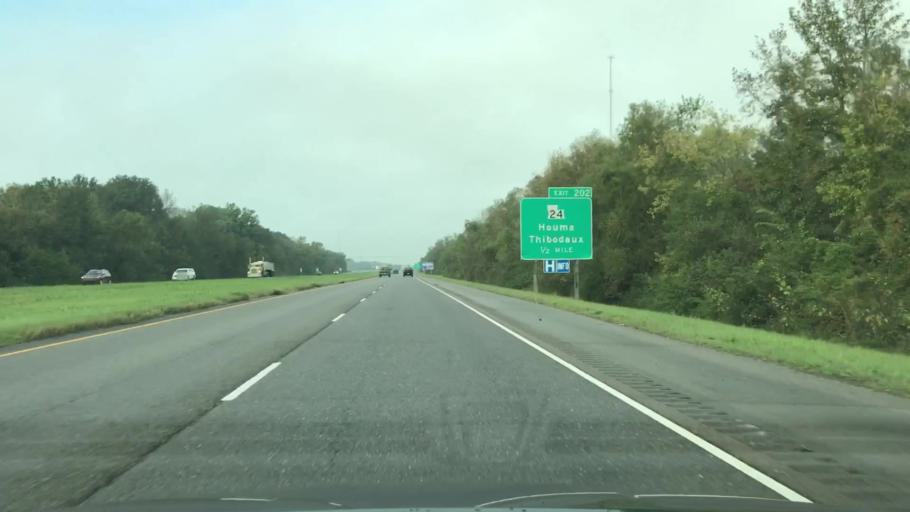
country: US
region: Louisiana
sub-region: Terrebonne Parish
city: Gray
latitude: 29.6810
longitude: -90.7702
